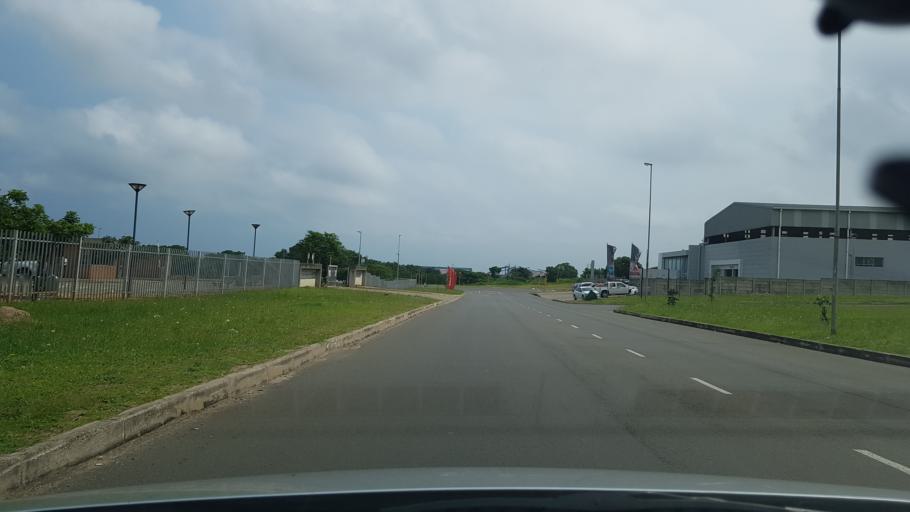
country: ZA
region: KwaZulu-Natal
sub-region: uThungulu District Municipality
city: Richards Bay
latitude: -28.7572
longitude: 32.0490
